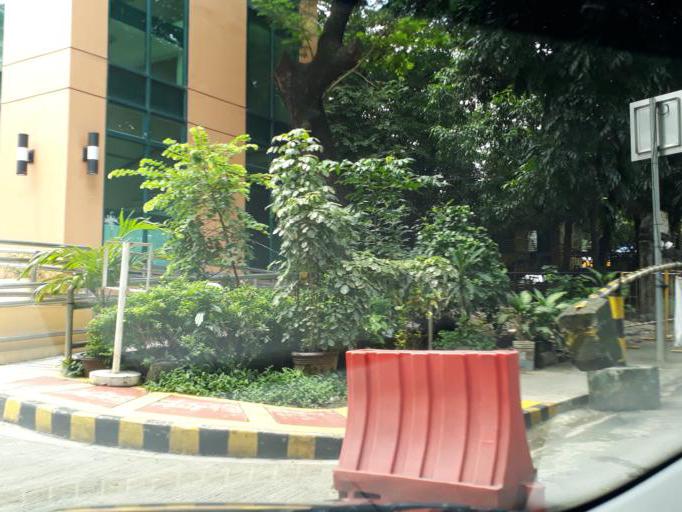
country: PH
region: Metro Manila
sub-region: Quezon City
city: Quezon City
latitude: 14.6475
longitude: 121.0518
